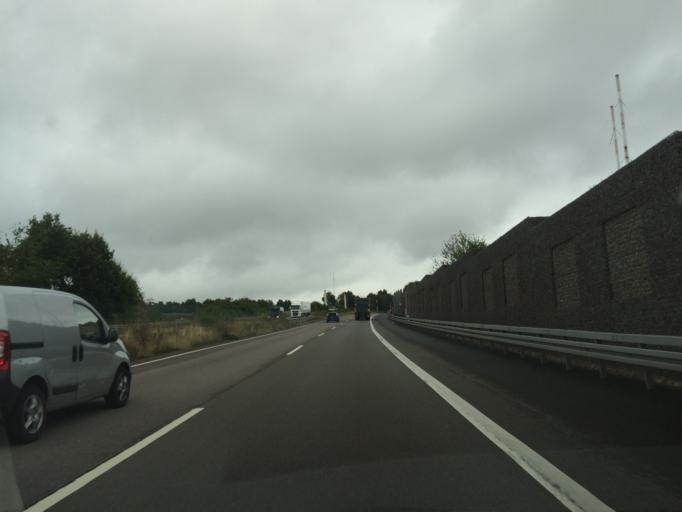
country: DE
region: Saarland
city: Heusweiler
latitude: 49.3436
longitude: 6.9092
